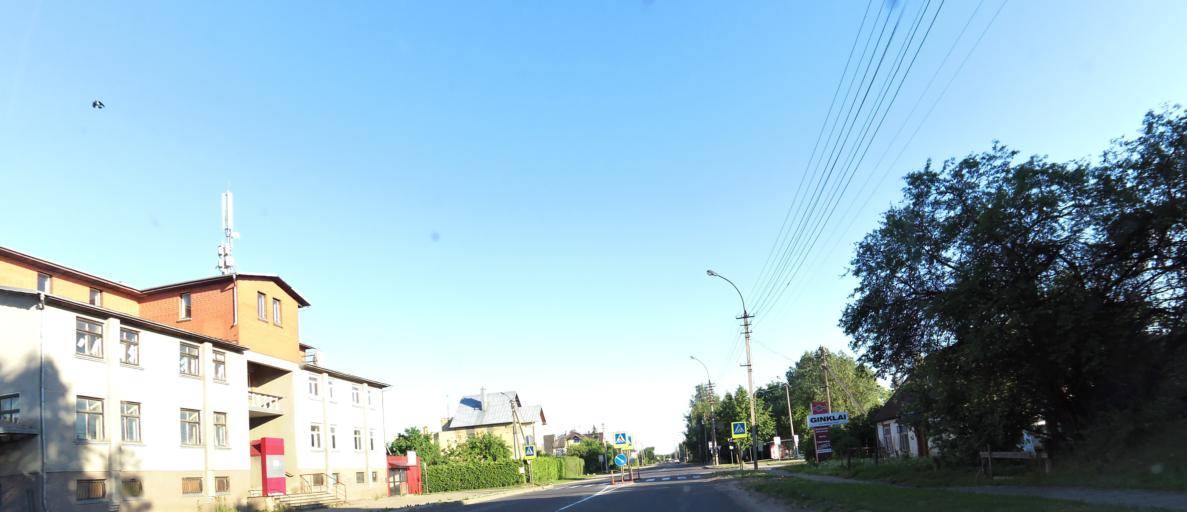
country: LT
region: Panevezys
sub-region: Panevezys City
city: Panevezys
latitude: 55.7556
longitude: 24.3689
